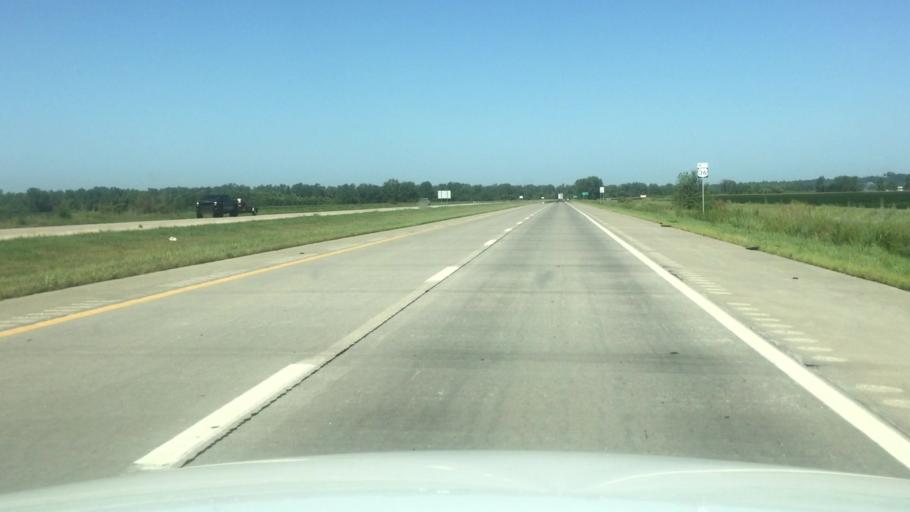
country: US
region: Kansas
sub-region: Doniphan County
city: Elwood
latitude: 39.7406
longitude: -94.9010
